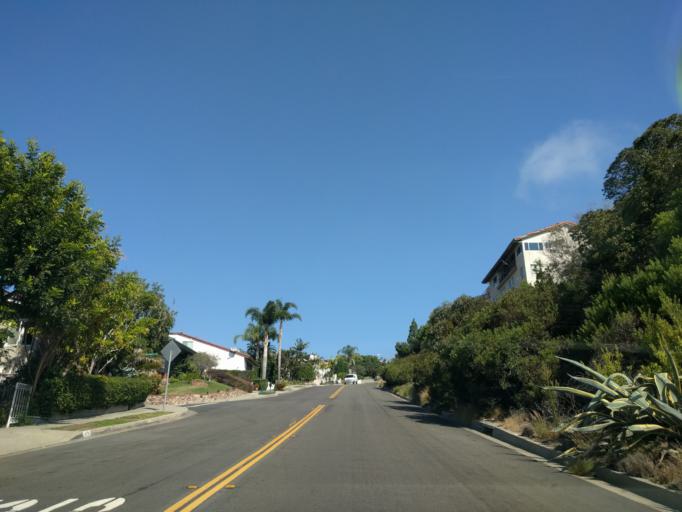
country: US
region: California
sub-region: Orange County
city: Laguna Beach
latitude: 33.5234
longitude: -117.7554
